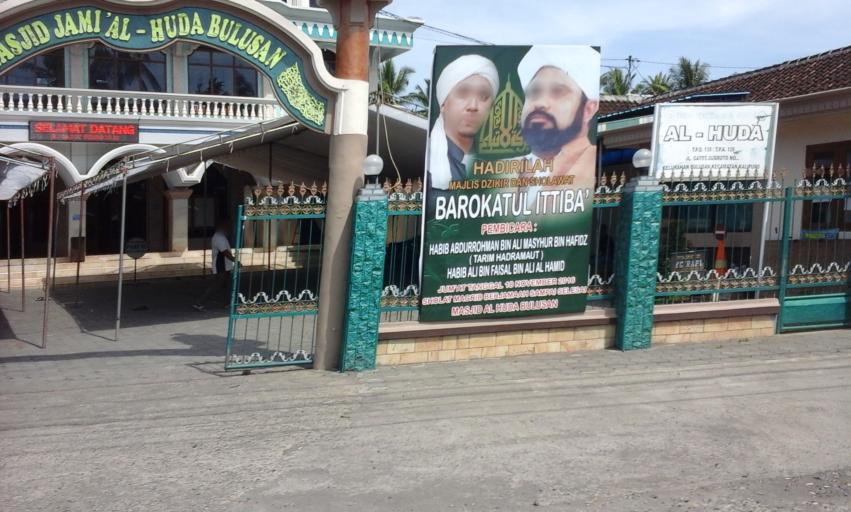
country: ID
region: East Java
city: Klatakan
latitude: -8.1587
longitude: 114.3922
